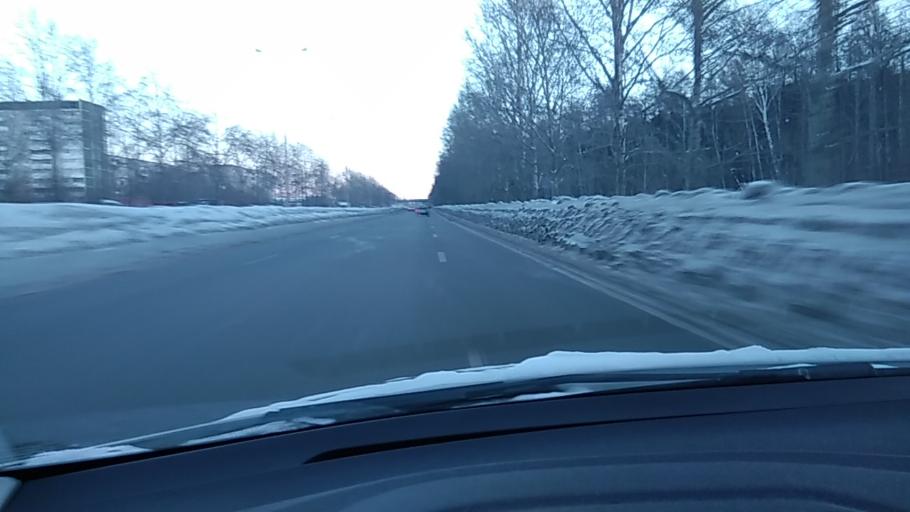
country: RU
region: Sverdlovsk
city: Sovkhoznyy
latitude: 56.8003
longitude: 60.5498
